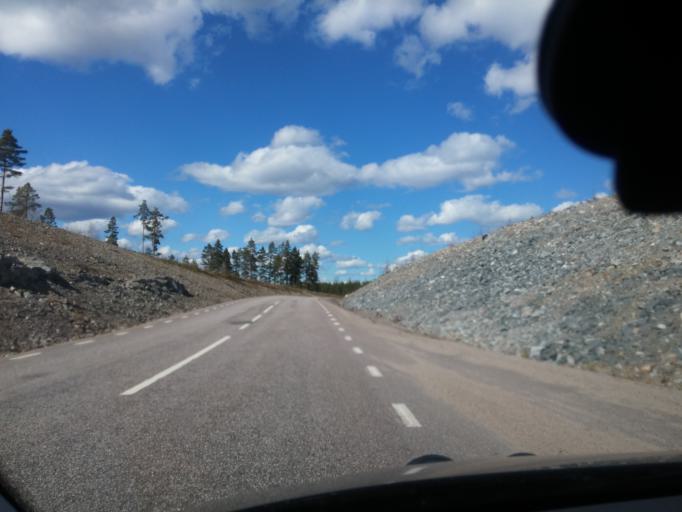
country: SE
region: Gaevleborg
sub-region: Ovanakers Kommun
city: Edsbyn
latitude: 61.2334
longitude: 15.8830
